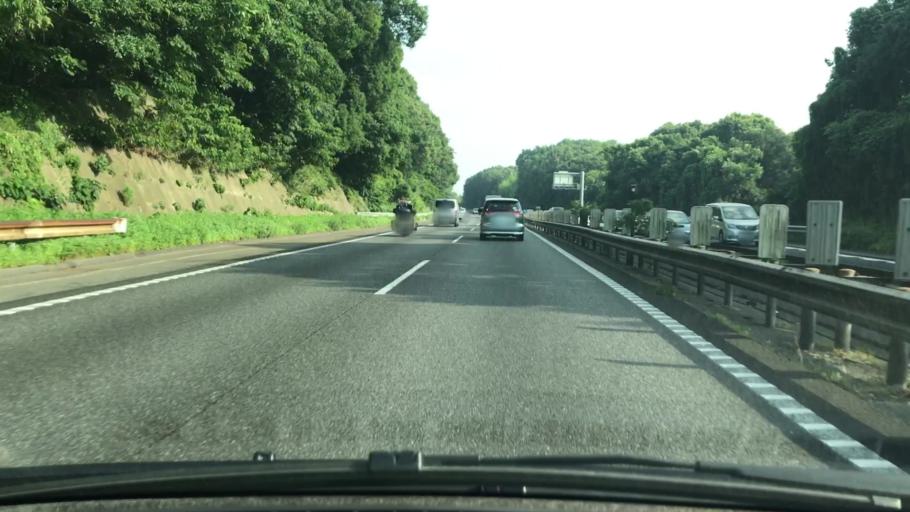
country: JP
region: Hyogo
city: Akashi
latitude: 34.6932
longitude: 134.9693
